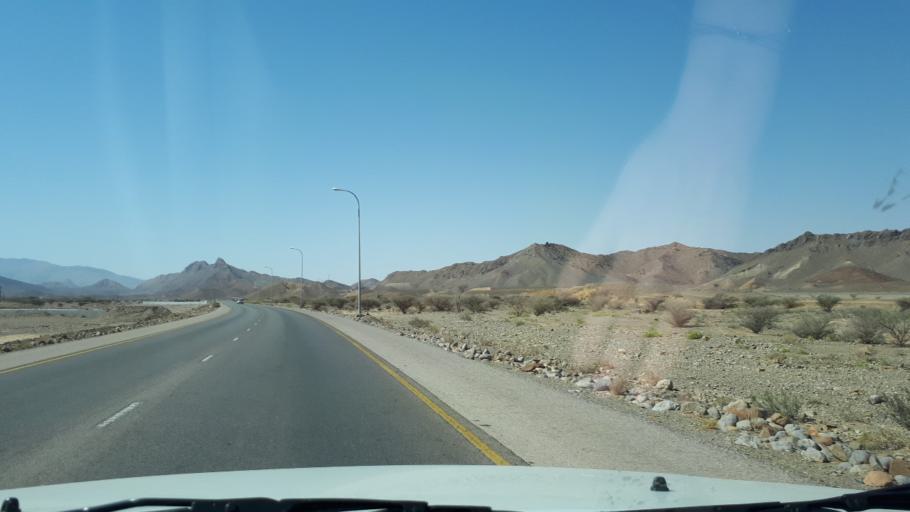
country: OM
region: Ash Sharqiyah
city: Sur
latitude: 22.3618
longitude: 59.3124
